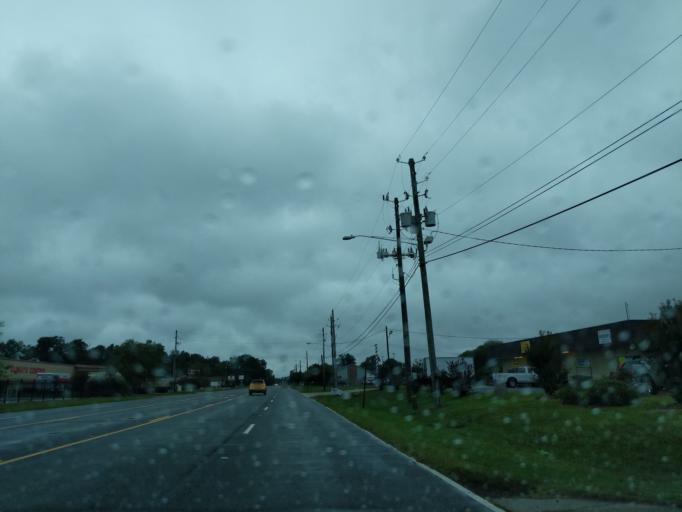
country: US
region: Louisiana
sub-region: Bossier Parish
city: Bossier City
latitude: 32.5133
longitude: -93.6847
